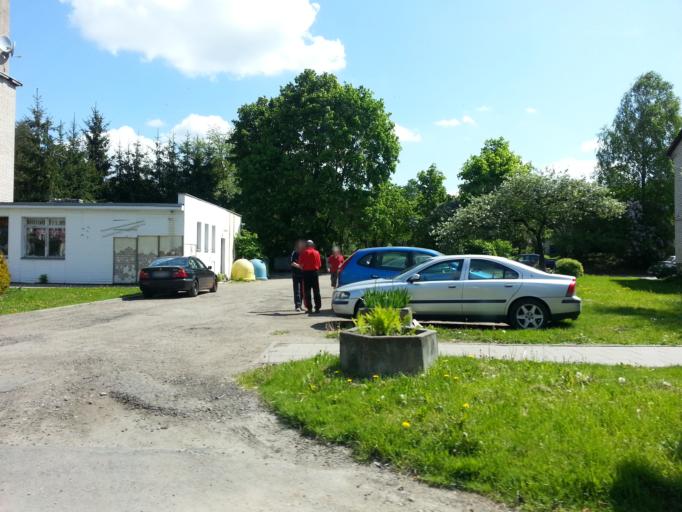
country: LT
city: Grigiskes
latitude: 54.6281
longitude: 25.1082
